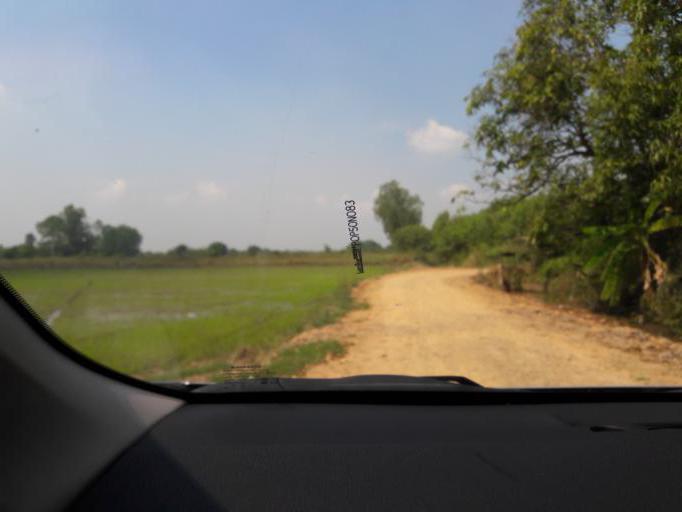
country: TH
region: Ang Thong
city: Ang Thong
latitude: 14.5603
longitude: 100.4236
